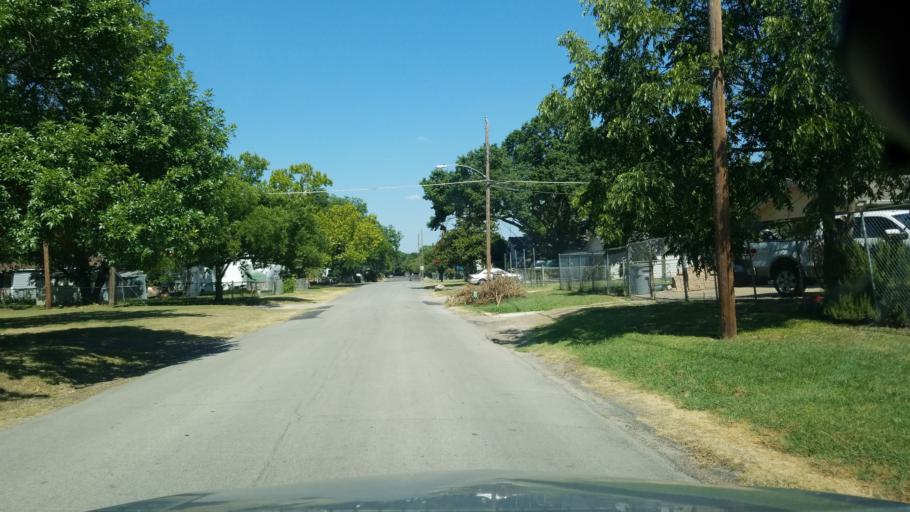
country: US
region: Texas
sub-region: Dallas County
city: Cockrell Hill
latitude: 32.7316
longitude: -96.8503
